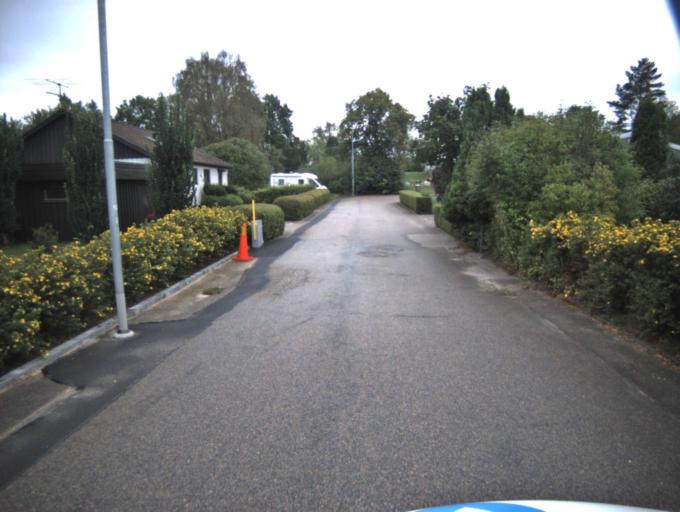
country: SE
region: Vaestra Goetaland
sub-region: Ulricehamns Kommun
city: Ulricehamn
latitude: 57.9213
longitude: 13.4914
